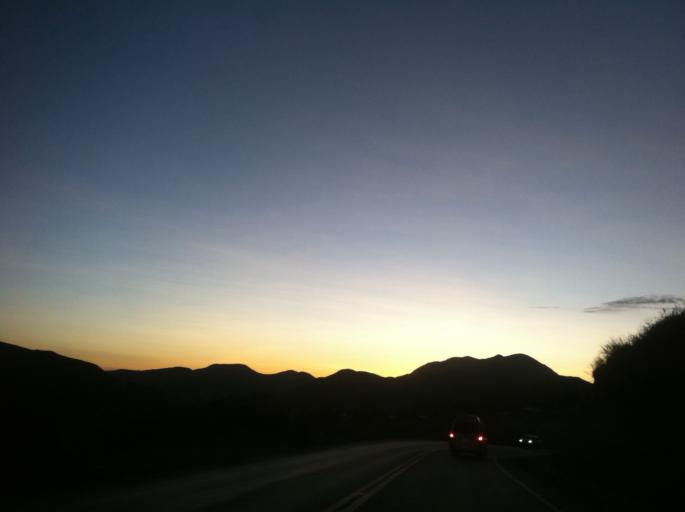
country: BO
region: Cochabamba
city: Irpa Irpa
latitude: -17.6637
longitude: -66.4174
